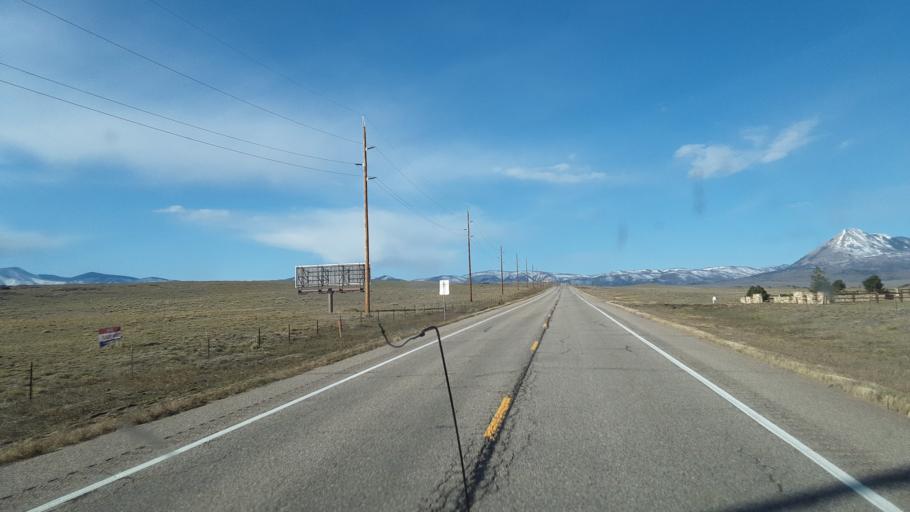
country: US
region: Colorado
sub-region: Huerfano County
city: Walsenburg
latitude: 37.5512
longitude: -104.9648
